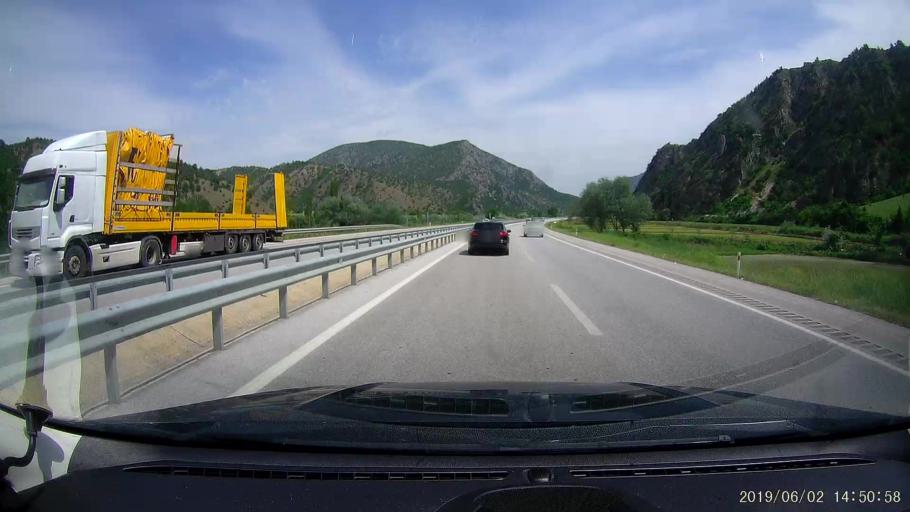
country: TR
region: Corum
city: Kargi
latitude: 41.0672
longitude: 34.5312
